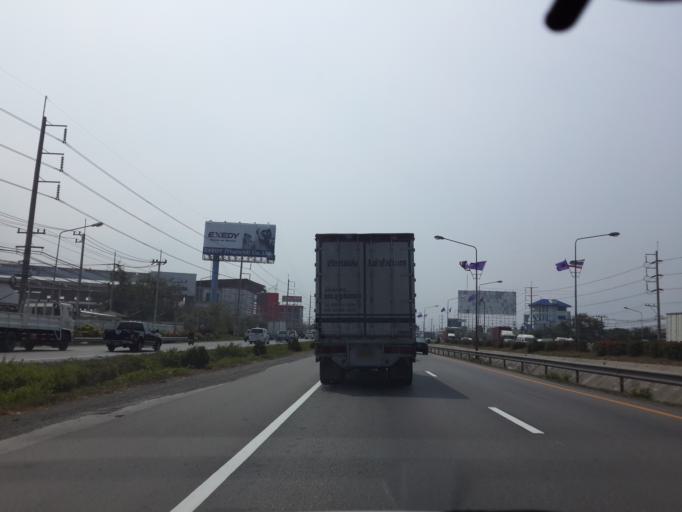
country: TH
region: Chon Buri
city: Chon Buri
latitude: 13.4461
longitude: 100.9995
